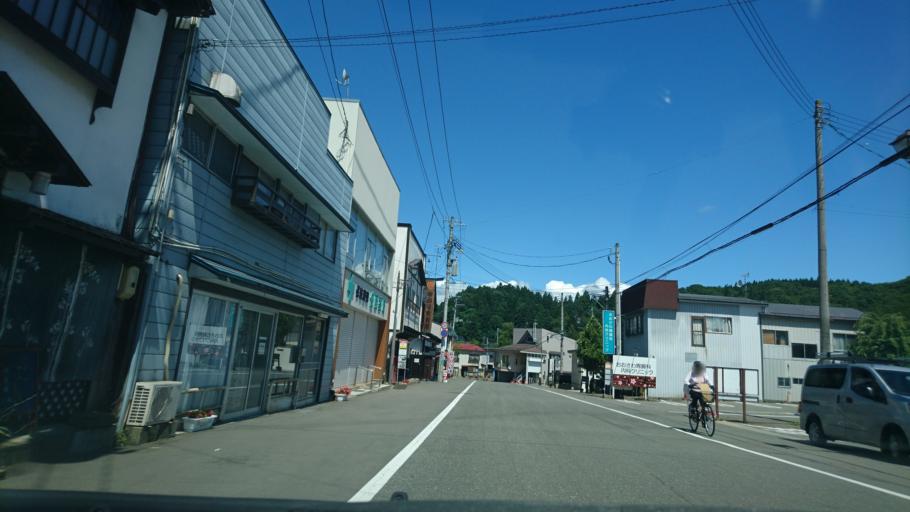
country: JP
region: Akita
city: Kakunodatemachi
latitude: 39.5929
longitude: 140.5688
